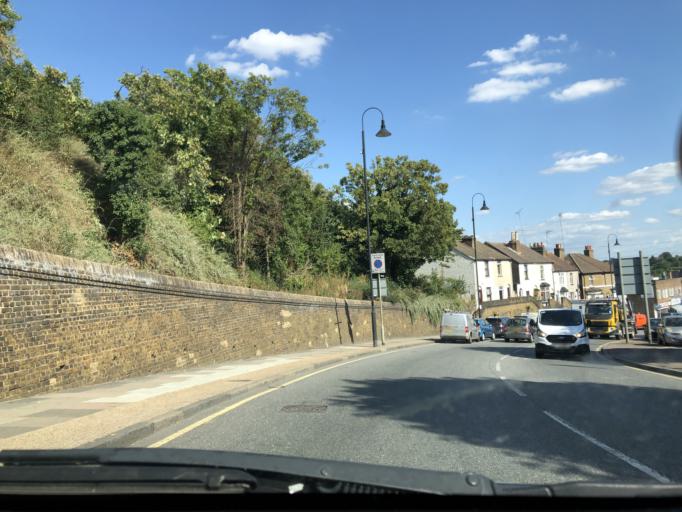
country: GB
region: England
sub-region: Greater London
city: Erith
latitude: 51.4540
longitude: 0.1756
